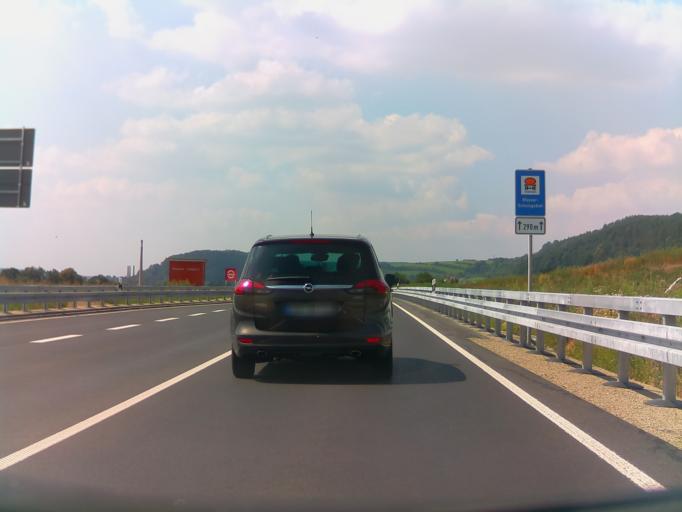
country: DE
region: Thuringia
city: Schops
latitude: 50.8293
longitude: 11.5908
